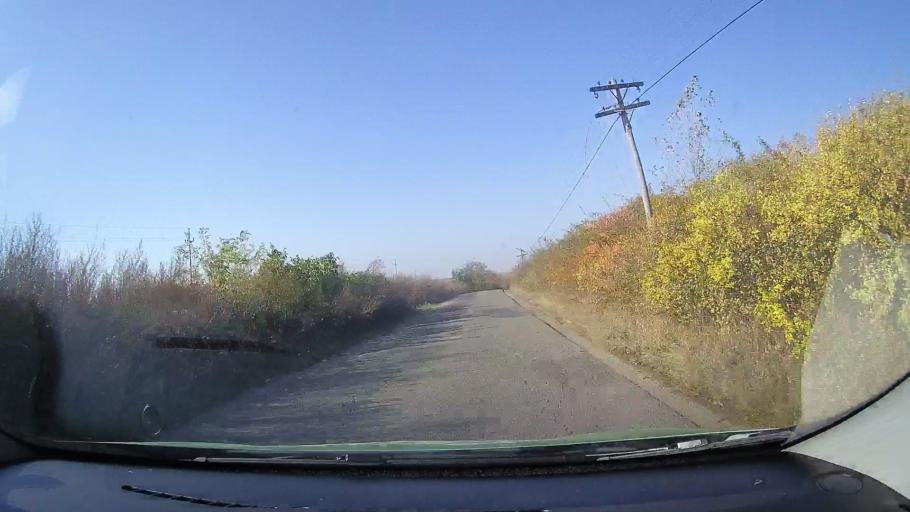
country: RO
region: Satu Mare
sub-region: Comuna Sauca
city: Sauca
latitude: 47.4681
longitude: 22.5077
